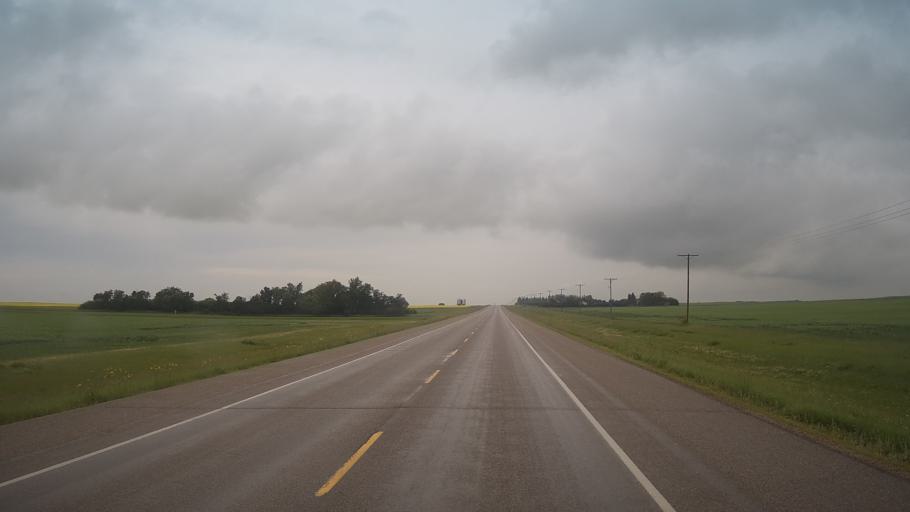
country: CA
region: Saskatchewan
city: Wilkie
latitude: 52.4056
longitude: -108.7770
